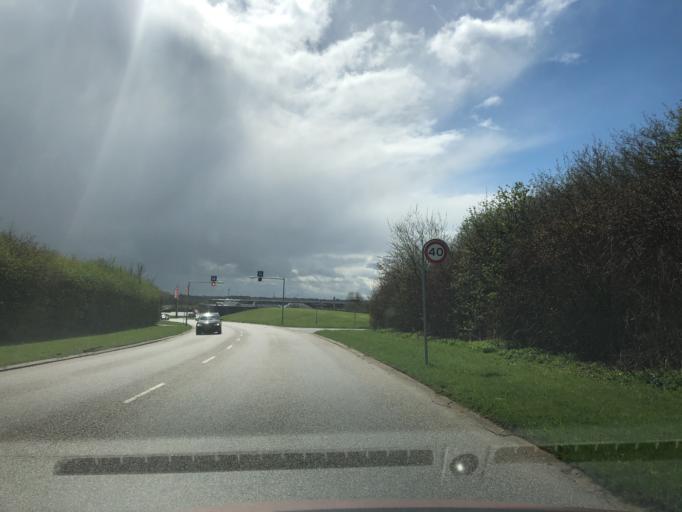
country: DK
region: South Denmark
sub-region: Kolding Kommune
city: Christiansfeld
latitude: 55.3588
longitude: 9.4951
